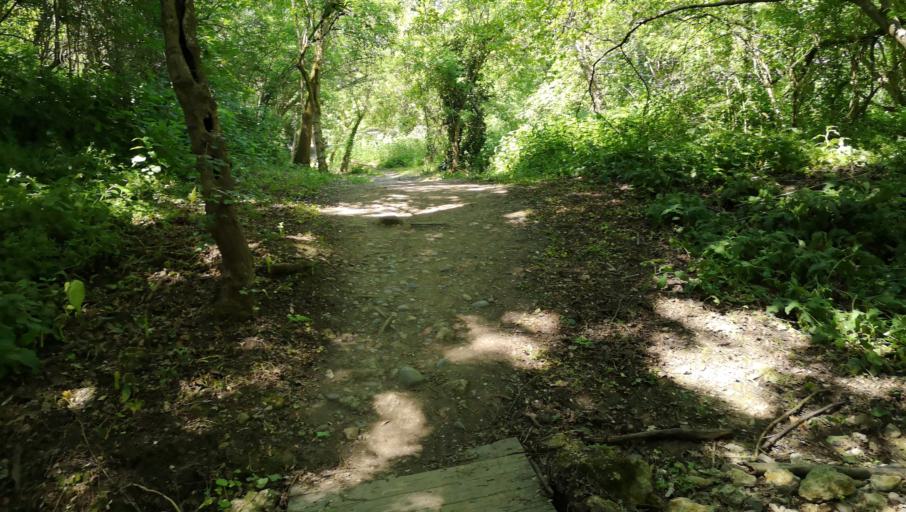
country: FR
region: Midi-Pyrenees
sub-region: Departement de la Haute-Garonne
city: Beauzelle
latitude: 43.6616
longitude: 1.3918
